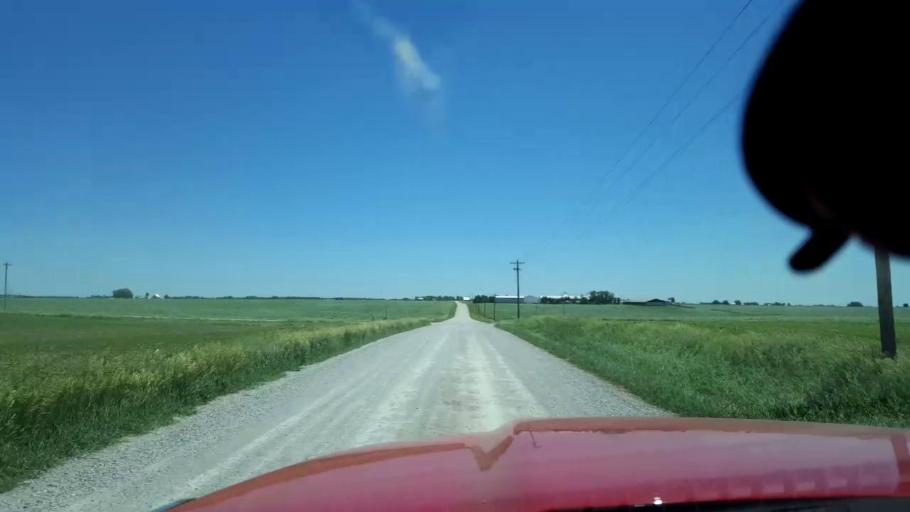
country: US
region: Iowa
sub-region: Washington County
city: Washington
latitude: 41.2799
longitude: -91.6457
